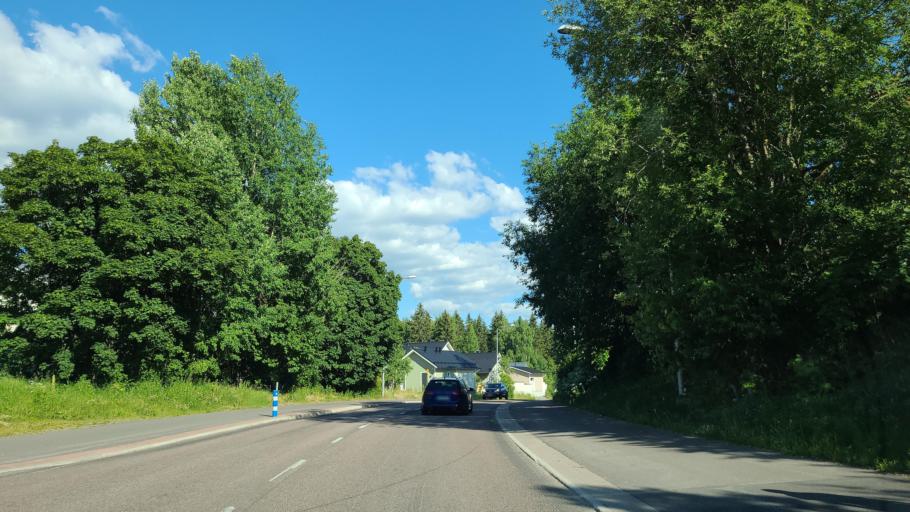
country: FI
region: Central Finland
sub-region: Jyvaeskylae
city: Jyvaeskylae
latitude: 62.2432
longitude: 25.7977
